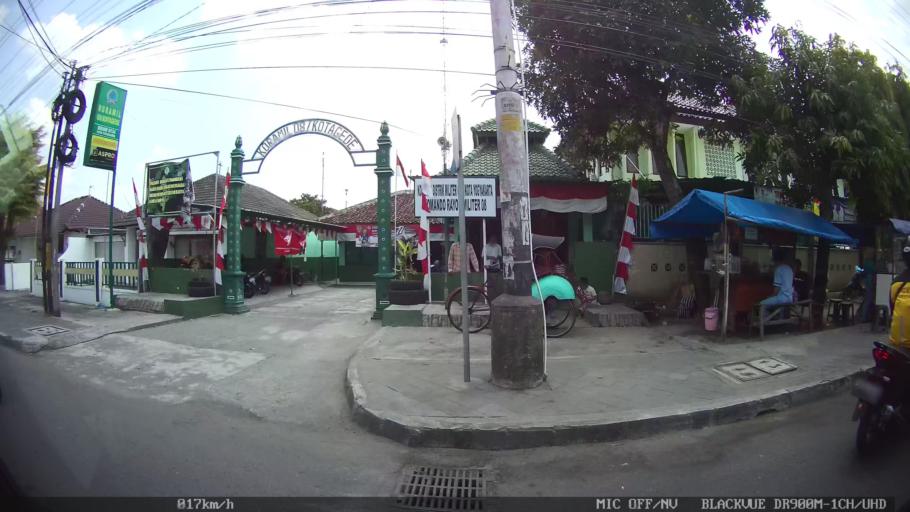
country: ID
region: Daerah Istimewa Yogyakarta
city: Yogyakarta
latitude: -7.8221
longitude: 110.4006
